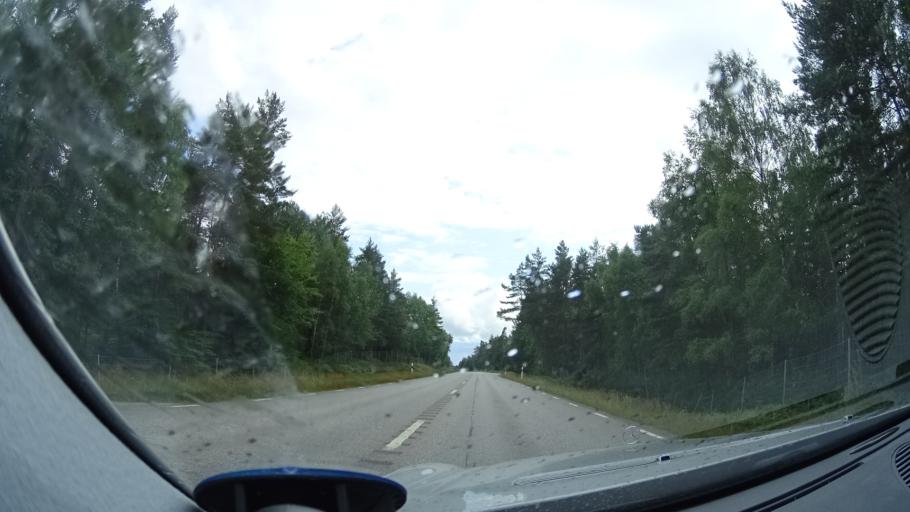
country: SE
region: Blekinge
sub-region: Karlshamns Kommun
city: Svangsta
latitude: 56.2479
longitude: 14.8289
